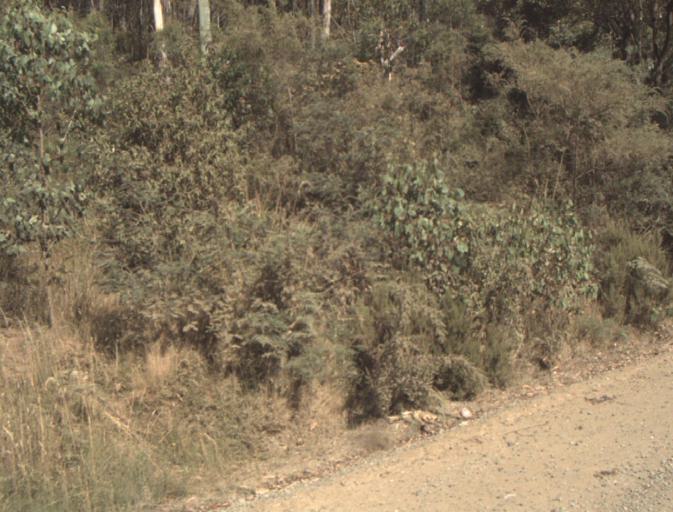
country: AU
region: Tasmania
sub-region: Launceston
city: Newstead
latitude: -41.3784
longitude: 147.2884
